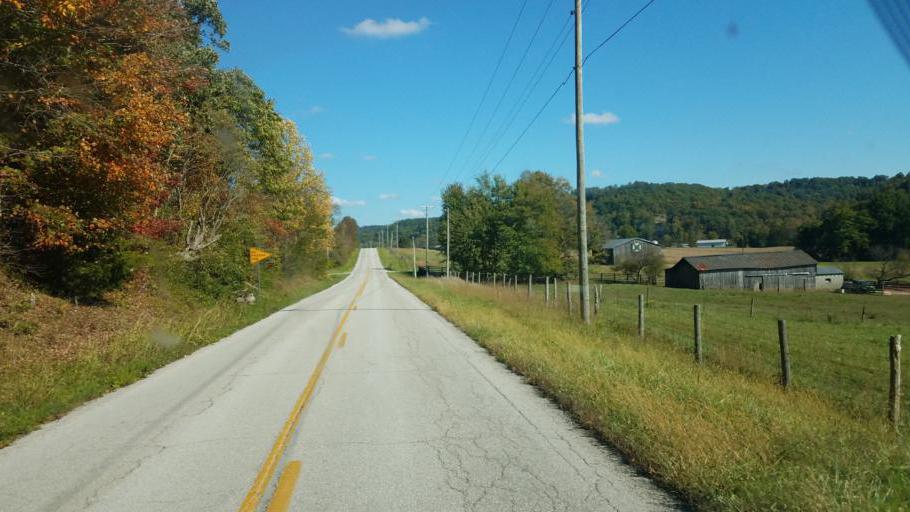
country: US
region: Kentucky
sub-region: Fleming County
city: Flemingsburg
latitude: 38.4683
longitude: -83.5460
